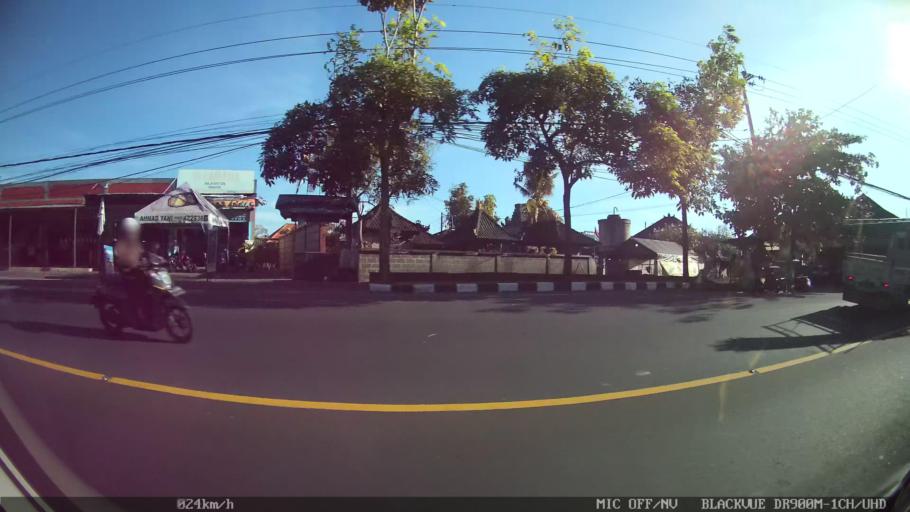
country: ID
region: Bali
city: Banjar Karangsuling
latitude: -8.6086
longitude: 115.1889
